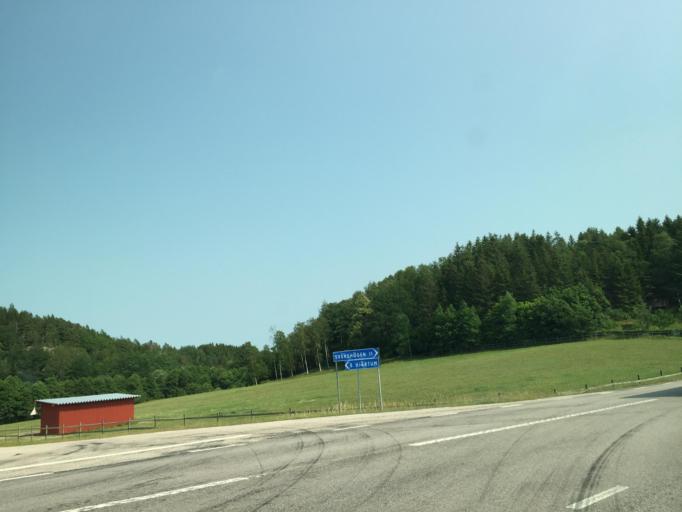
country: SE
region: Vaestra Goetaland
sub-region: Lilla Edets Kommun
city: Lilla Edet
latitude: 58.1530
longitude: 12.0539
